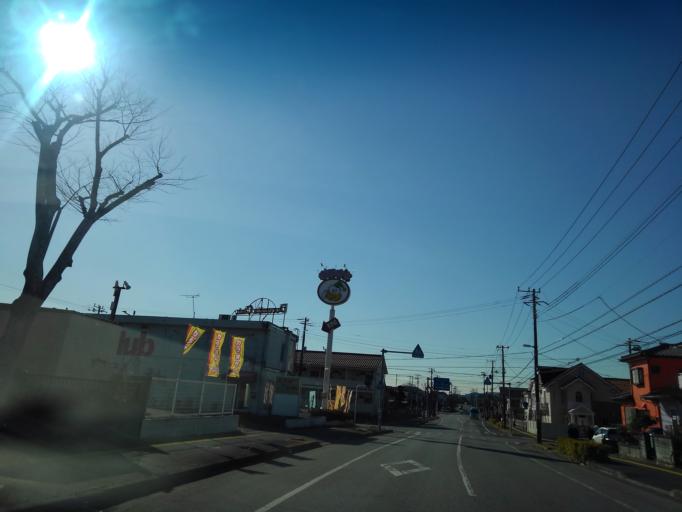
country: JP
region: Chiba
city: Kimitsu
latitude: 35.3337
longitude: 139.9171
